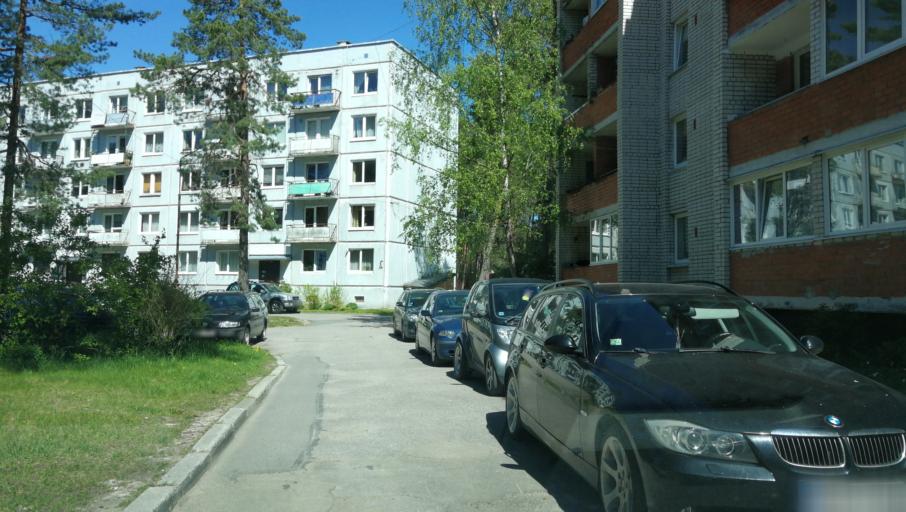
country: LV
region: Adazi
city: Adazi
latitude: 57.0910
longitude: 24.3612
